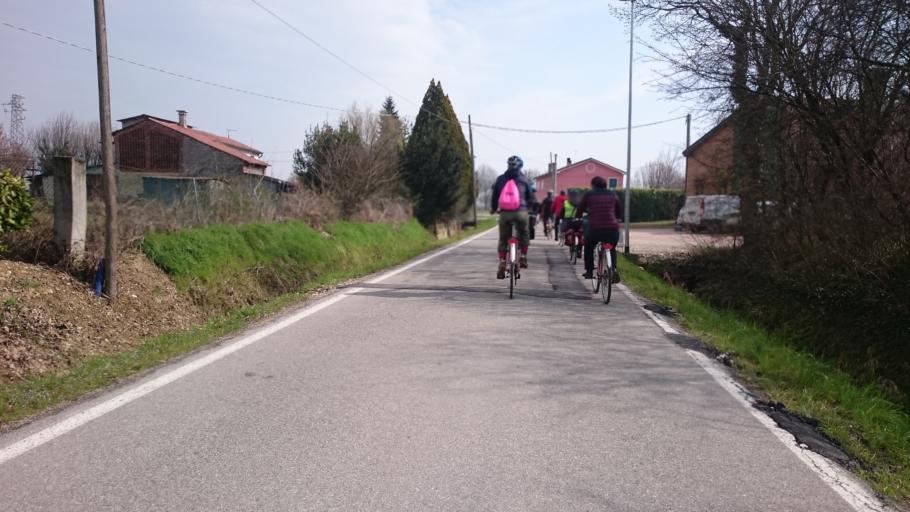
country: IT
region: Veneto
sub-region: Provincia di Vicenza
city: Villaganzerla
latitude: 45.4521
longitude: 11.6182
